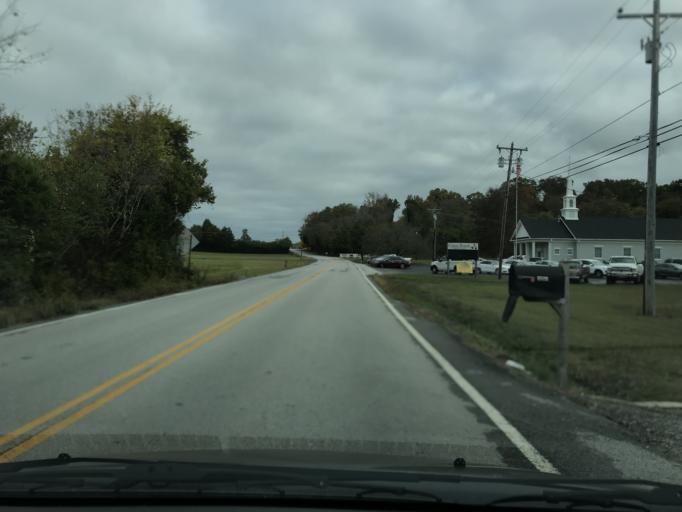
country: US
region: Tennessee
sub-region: Hamilton County
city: Lakesite
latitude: 35.1761
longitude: -85.0272
